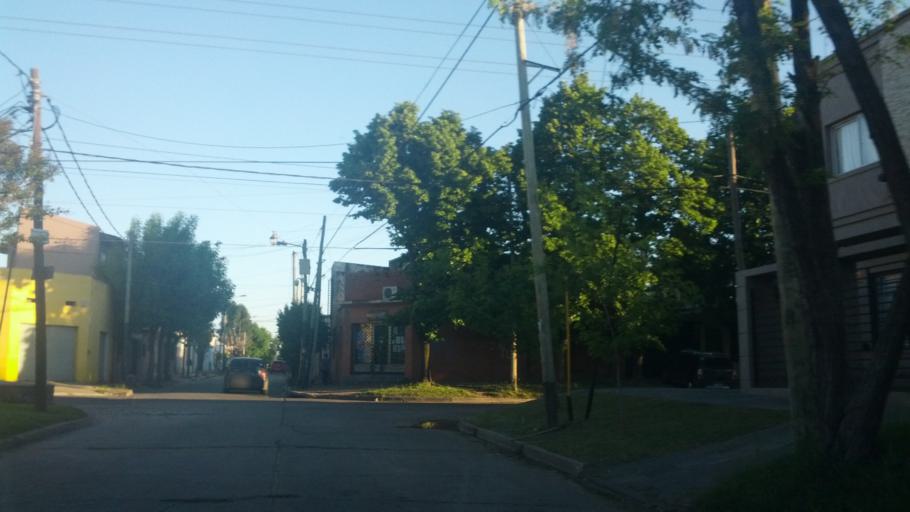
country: AR
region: Buenos Aires
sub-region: Partido de Lomas de Zamora
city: Lomas de Zamora
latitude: -34.7777
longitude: -58.4107
